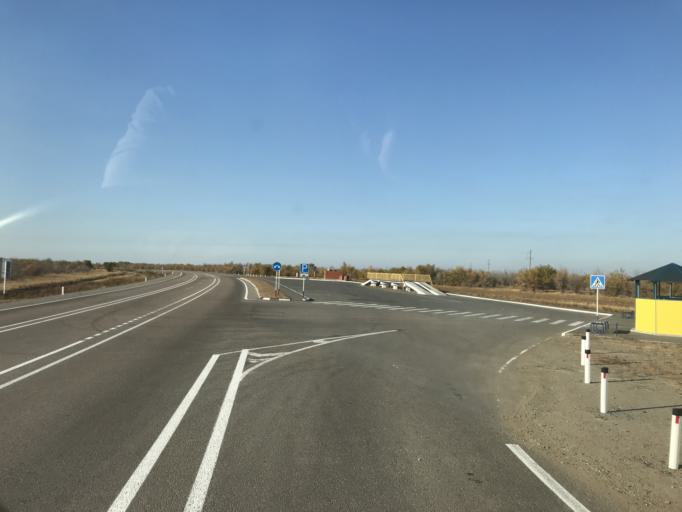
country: KZ
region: Pavlodar
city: Koktobe
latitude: 51.7273
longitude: 77.5600
